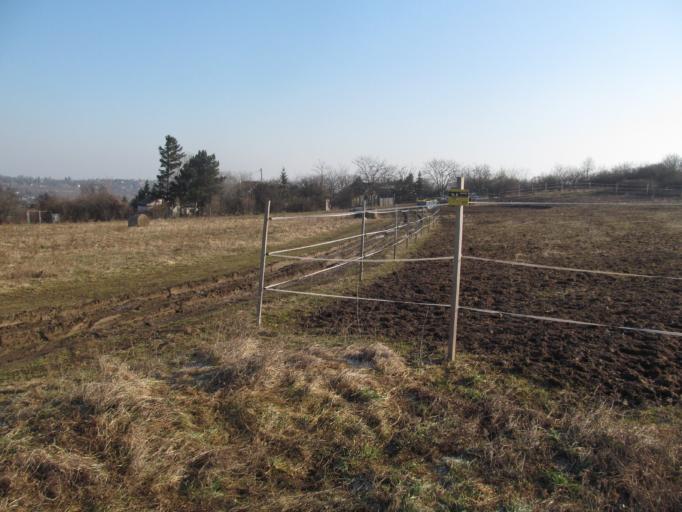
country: HU
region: Pest
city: Urom
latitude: 47.5993
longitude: 19.0299
